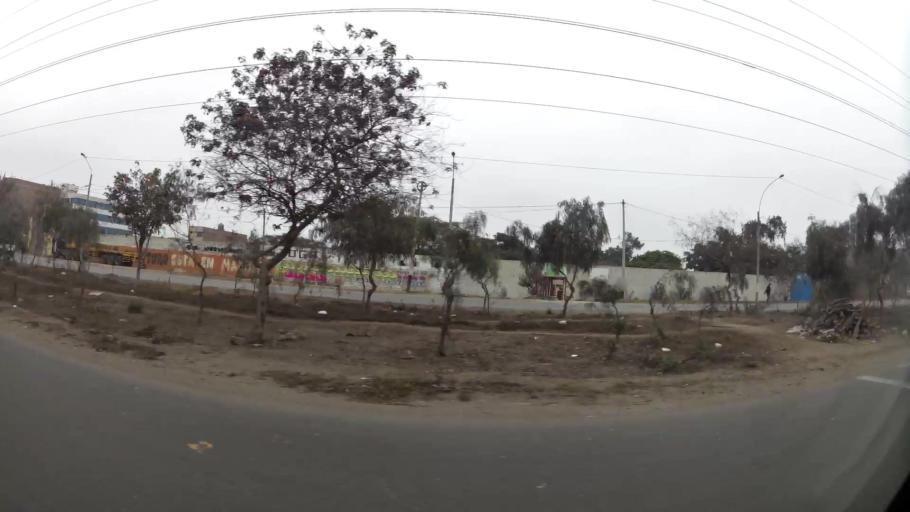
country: PE
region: Lima
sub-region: Lima
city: Urb. Santo Domingo
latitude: -11.9080
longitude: -77.0546
